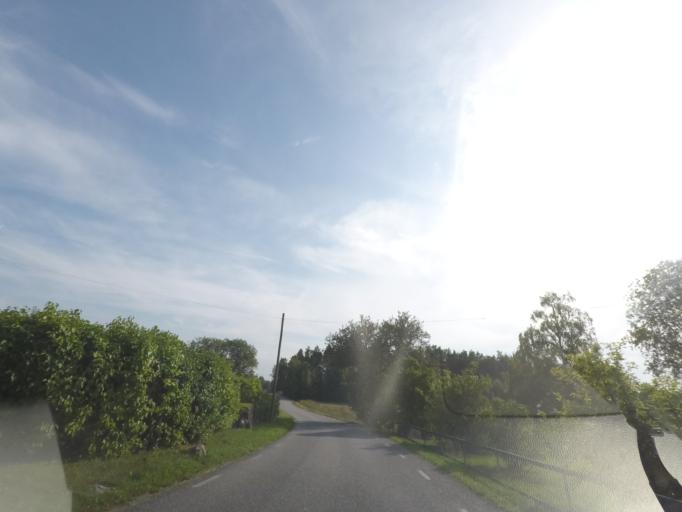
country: SE
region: Vaestmanland
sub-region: Kungsors Kommun
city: Kungsoer
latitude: 59.5213
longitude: 16.1459
